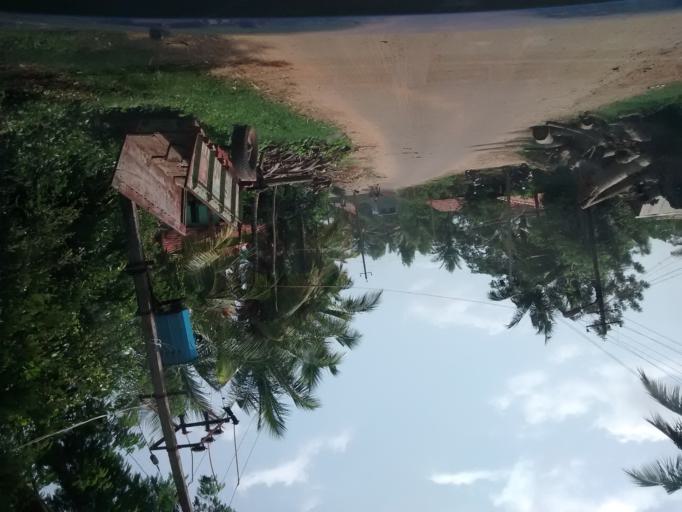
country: IN
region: Karnataka
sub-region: Hassan
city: Hole Narsipur
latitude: 12.7001
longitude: 76.1641
